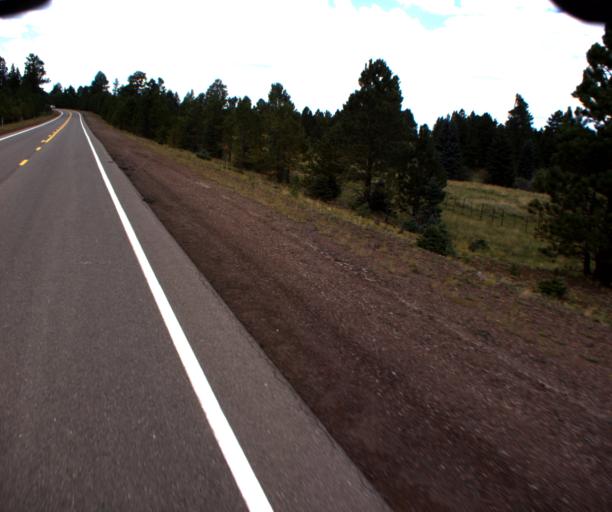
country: US
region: Arizona
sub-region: Apache County
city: Eagar
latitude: 34.0010
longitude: -109.5443
